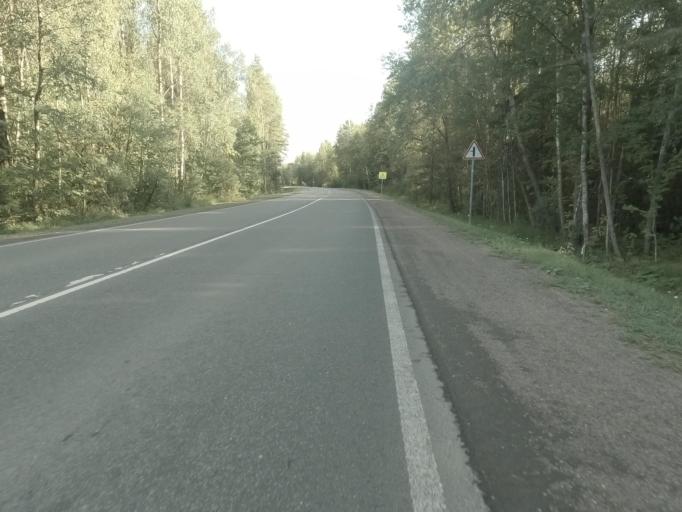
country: RU
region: Leningrad
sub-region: Volosovskiy Rayon
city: Shlissel'burg
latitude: 59.9402
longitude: 30.9826
